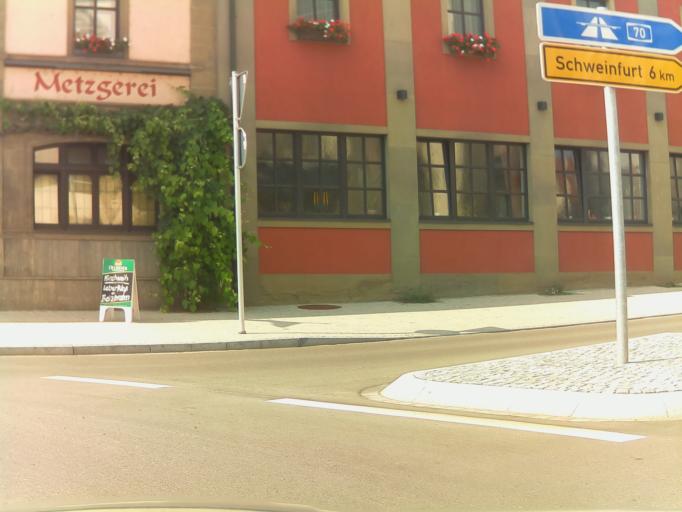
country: DE
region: Bavaria
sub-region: Regierungsbezirk Unterfranken
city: Bergrheinfeld
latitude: 50.0065
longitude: 10.1806
